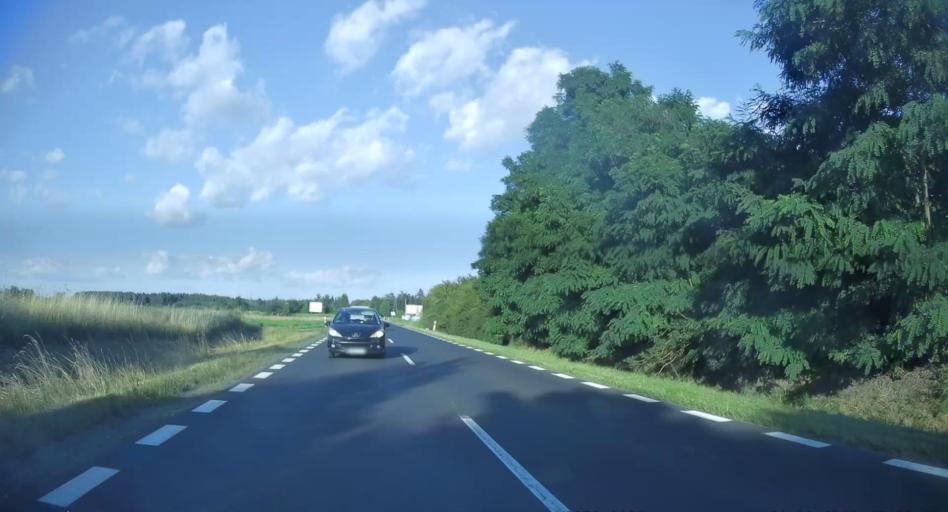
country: PL
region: Lodz Voivodeship
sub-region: Powiat rawski
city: Rawa Mazowiecka
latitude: 51.7742
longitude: 20.2817
